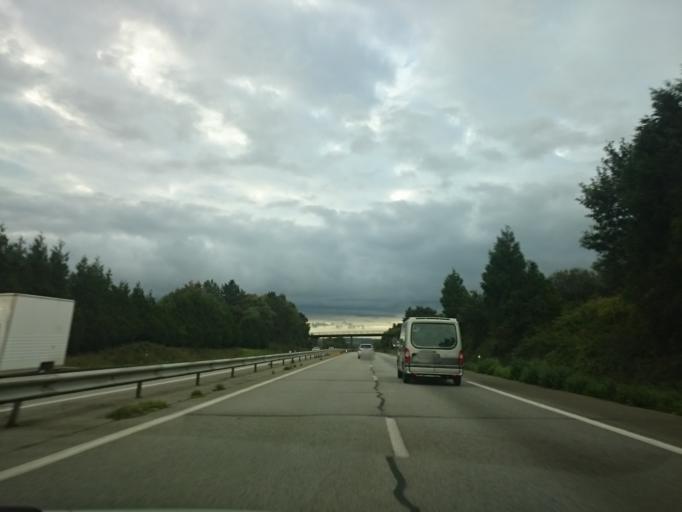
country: FR
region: Brittany
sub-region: Departement du Finistere
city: Briec
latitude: 48.1529
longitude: -4.0371
